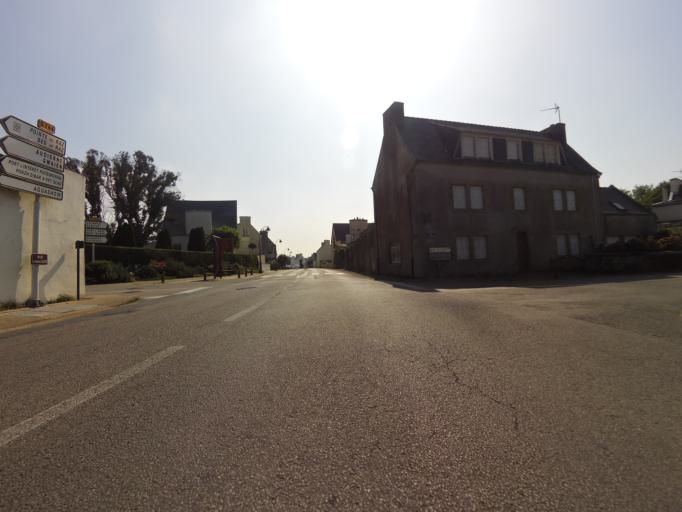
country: FR
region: Brittany
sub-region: Departement du Finistere
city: Plouhinec
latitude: 48.0140
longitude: -4.4844
